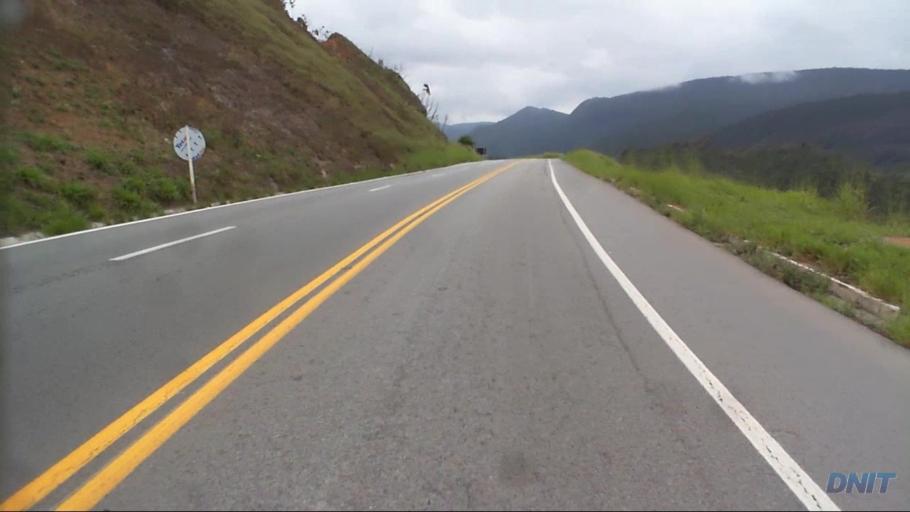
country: BR
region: Minas Gerais
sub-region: Nova Era
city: Nova Era
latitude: -19.6412
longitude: -42.9014
